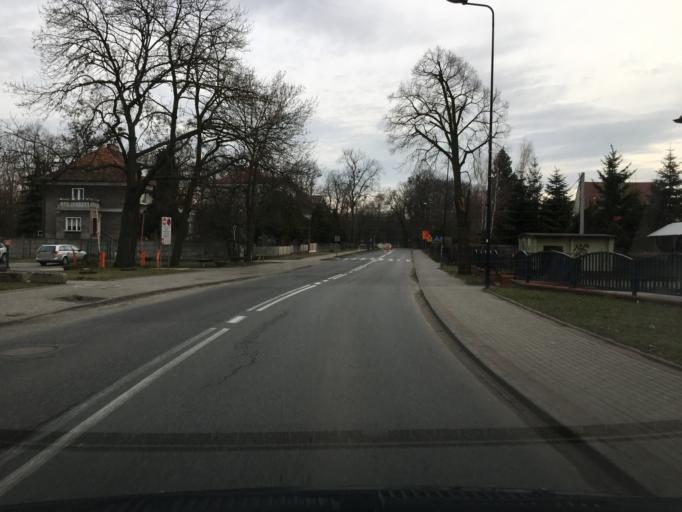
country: PL
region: Opole Voivodeship
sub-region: Powiat kedzierzynsko-kozielski
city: Kozle
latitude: 50.3316
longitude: 18.1497
